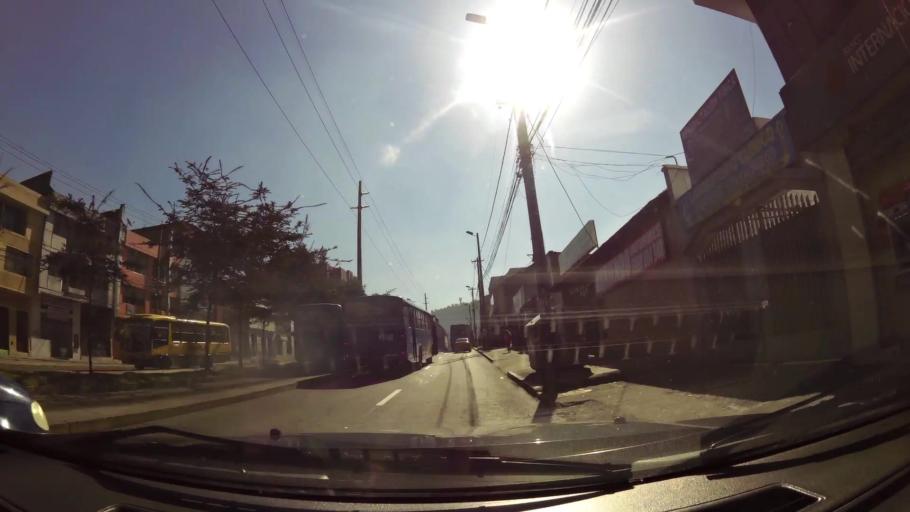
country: EC
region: Pichincha
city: Quito
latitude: -0.2388
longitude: -78.5300
